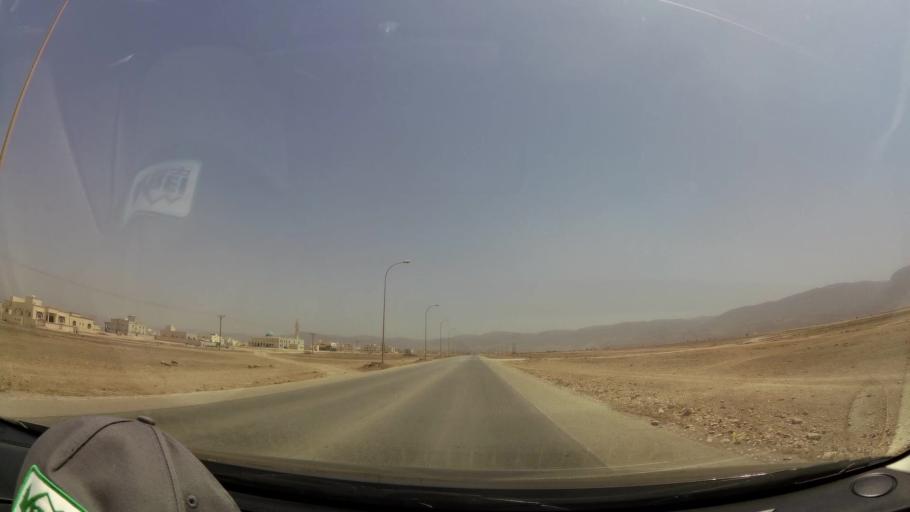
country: OM
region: Zufar
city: Salalah
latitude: 17.0786
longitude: 54.2171
